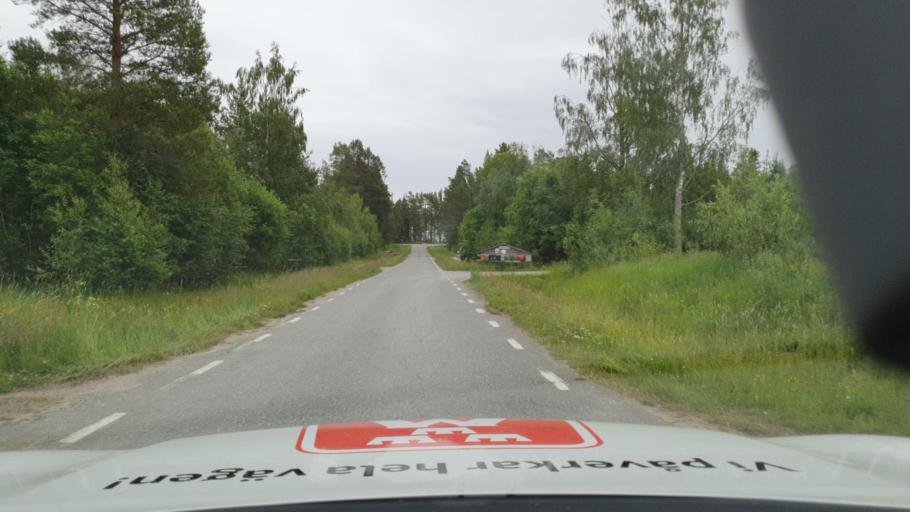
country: SE
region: Vaesterbotten
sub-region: Nordmalings Kommun
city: Nordmaling
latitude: 63.4252
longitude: 19.4977
